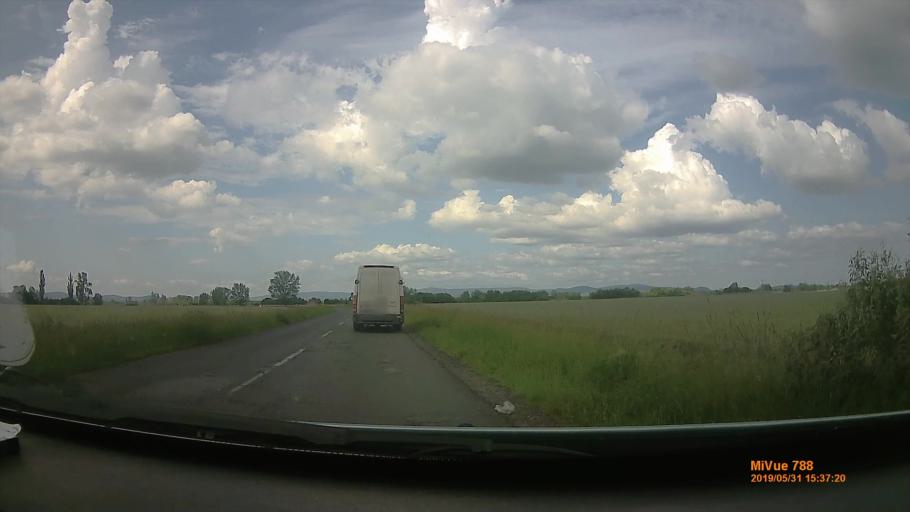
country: HU
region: Borsod-Abauj-Zemplen
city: Prugy
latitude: 48.0910
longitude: 21.2414
